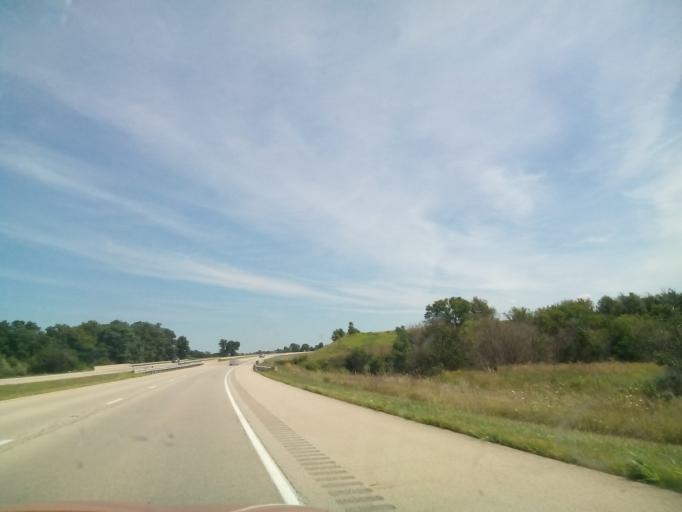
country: US
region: Illinois
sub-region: Winnebago County
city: Pecatonica
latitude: 42.2859
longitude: -89.3936
